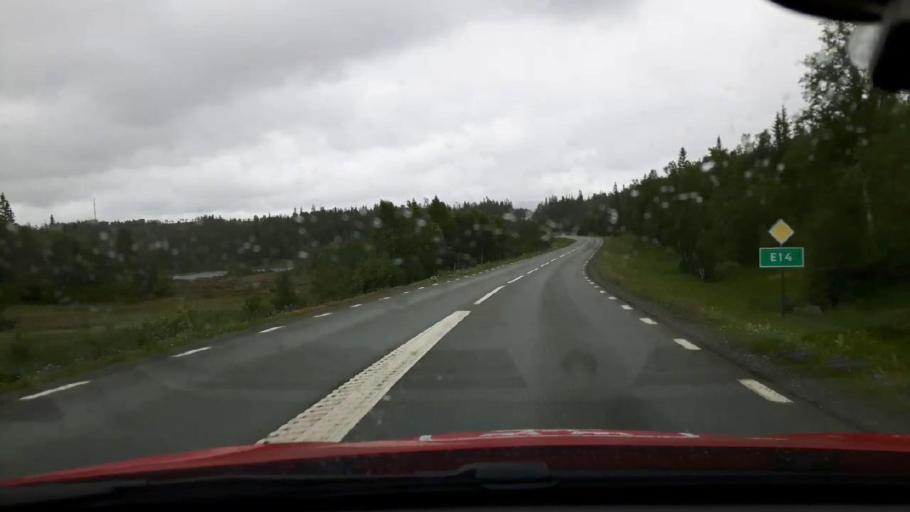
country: NO
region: Nord-Trondelag
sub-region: Meraker
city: Meraker
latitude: 63.3084
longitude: 12.1088
